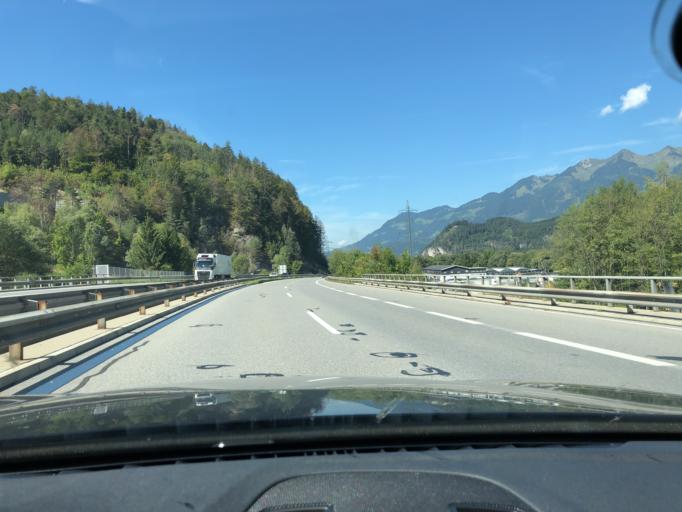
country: AT
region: Vorarlberg
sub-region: Politischer Bezirk Bludenz
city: Nuziders
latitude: 47.1599
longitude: 9.7993
